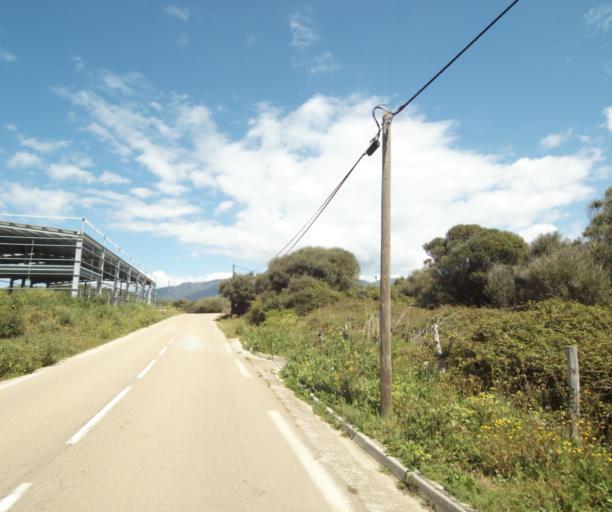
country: FR
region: Corsica
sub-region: Departement de la Corse-du-Sud
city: Propriano
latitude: 41.6570
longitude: 8.8938
